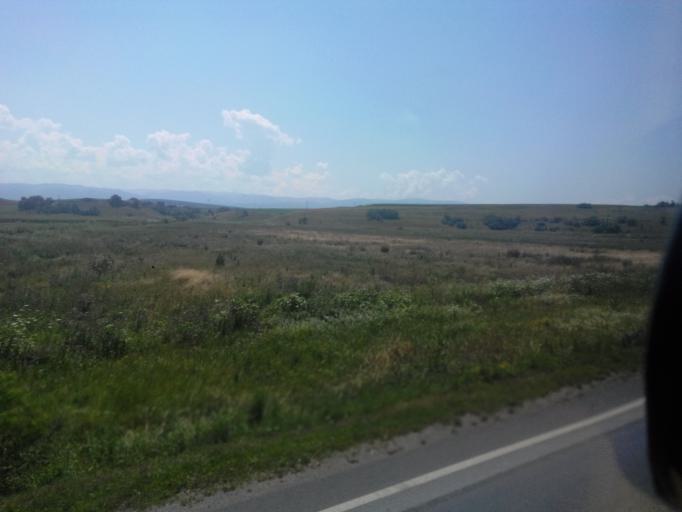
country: RO
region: Hunedoara
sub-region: Municipiul Orastie
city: Orastie
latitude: 45.8712
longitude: 23.2307
